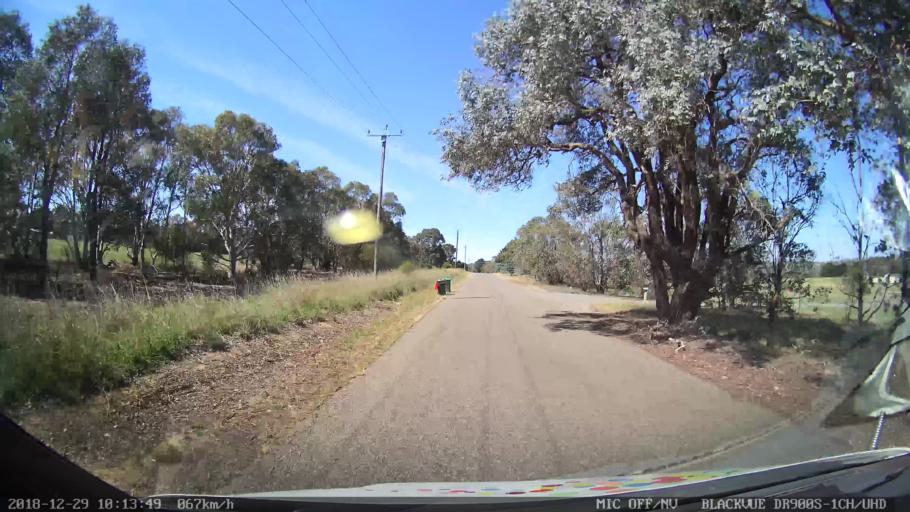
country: AU
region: New South Wales
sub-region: Yass Valley
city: Gundaroo
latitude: -34.9068
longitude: 149.4418
